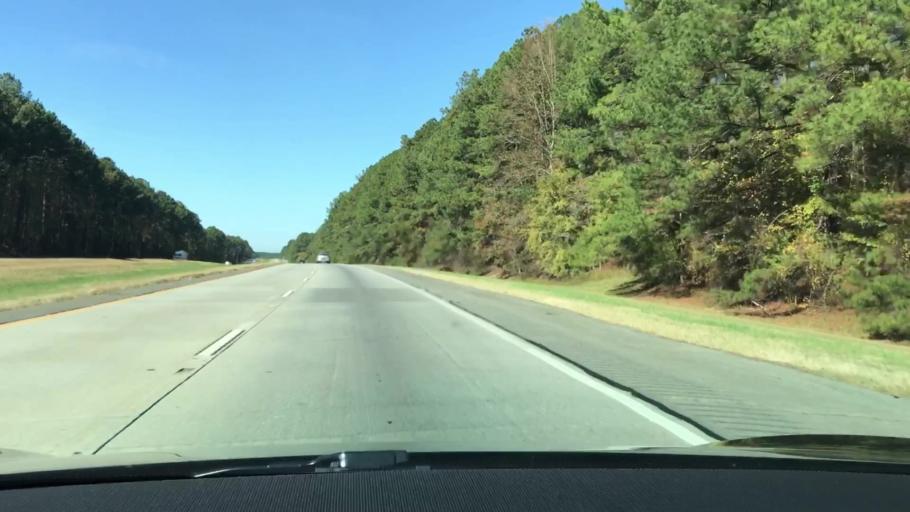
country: US
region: Georgia
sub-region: Taliaferro County
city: Crawfordville
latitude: 33.5242
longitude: -82.8762
